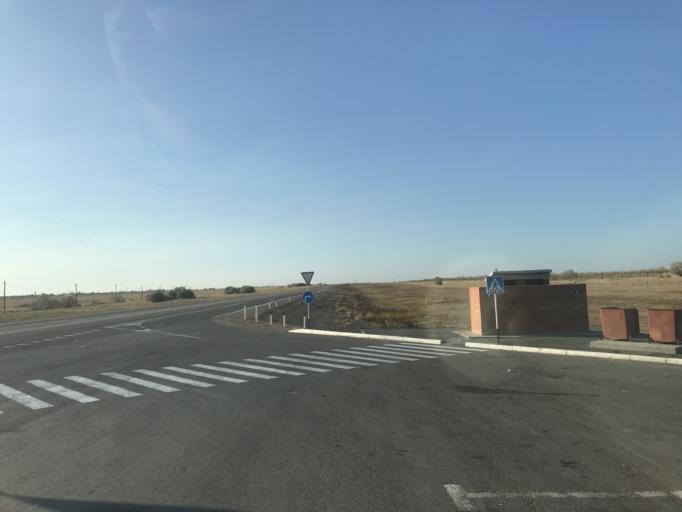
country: KZ
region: Pavlodar
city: Koktobe
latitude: 51.8830
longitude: 77.4184
